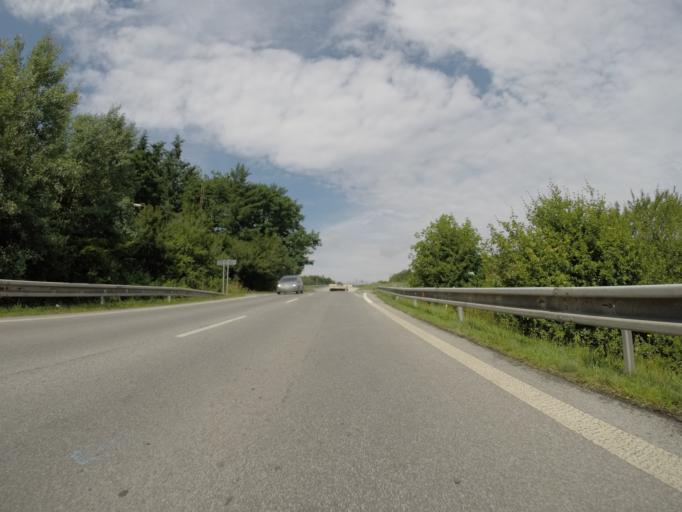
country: SK
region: Banskobystricky
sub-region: Okres Banska Bystrica
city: Zvolen
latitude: 48.5850
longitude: 19.0932
